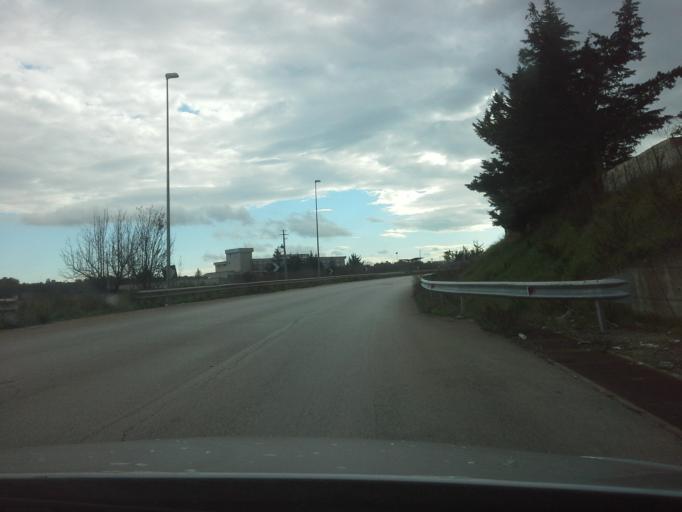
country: IT
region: Apulia
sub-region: Provincia di Bari
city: Turi
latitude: 40.9240
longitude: 16.9989
